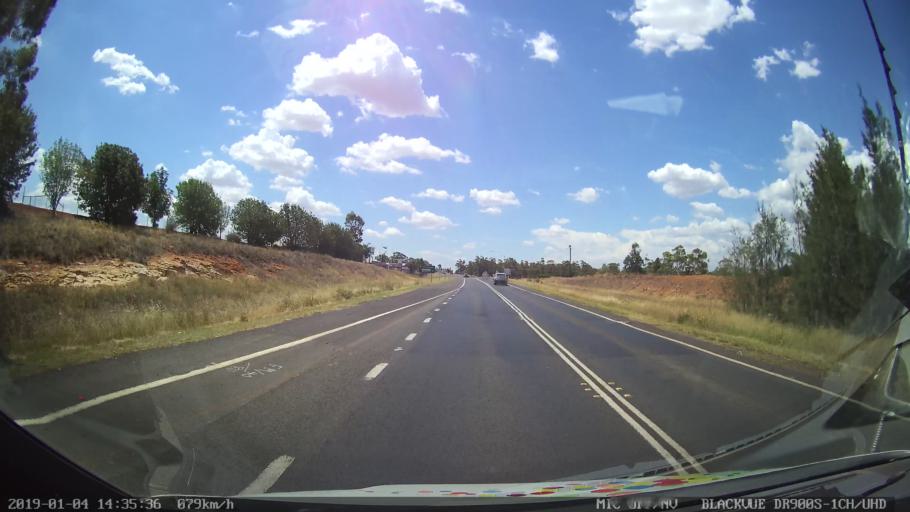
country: AU
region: New South Wales
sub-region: Dubbo Municipality
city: Dubbo
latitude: -32.1839
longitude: 148.6220
